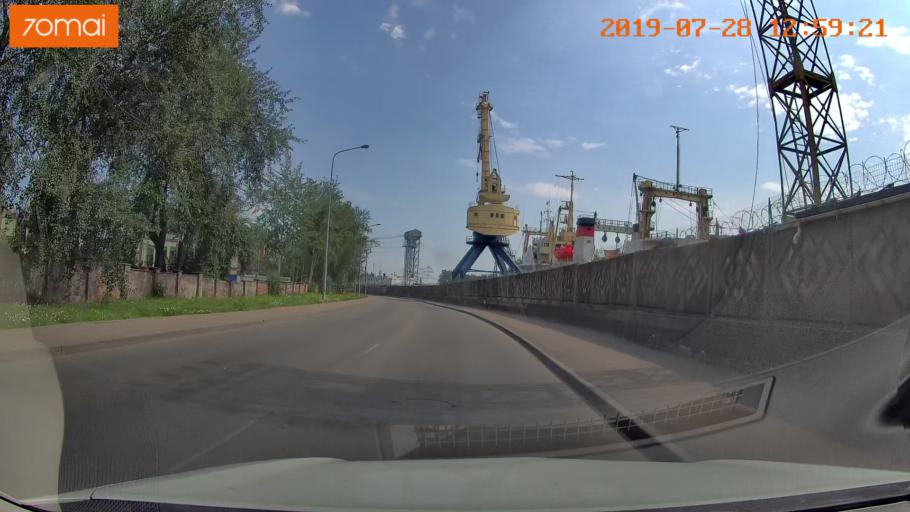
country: RU
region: Kaliningrad
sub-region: Gorod Kaliningrad
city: Kaliningrad
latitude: 54.7048
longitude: 20.4835
